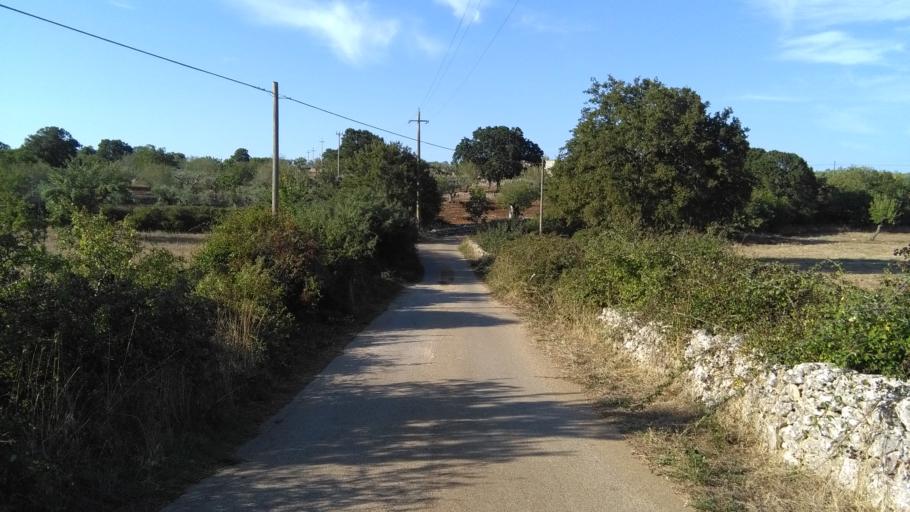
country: IT
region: Apulia
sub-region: Provincia di Bari
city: Putignano
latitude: 40.8292
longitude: 17.0591
